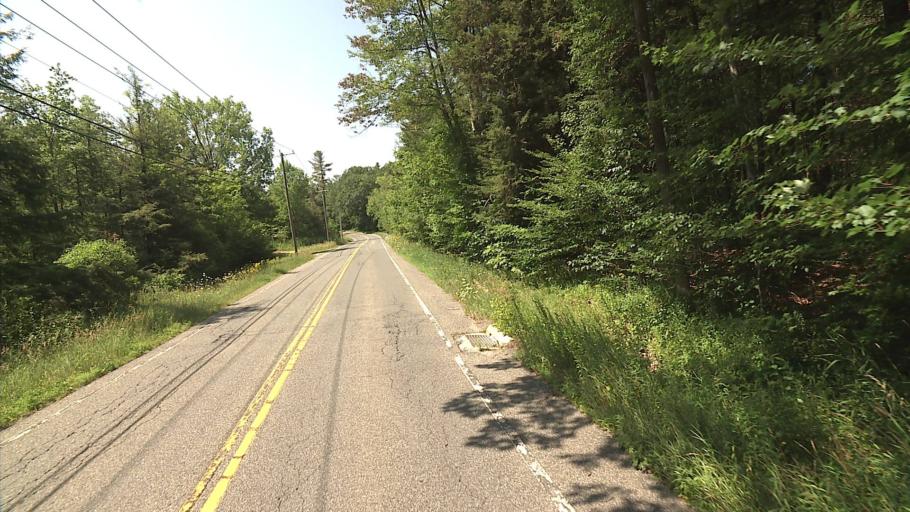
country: US
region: Connecticut
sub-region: Litchfield County
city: Winchester Center
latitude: 41.9506
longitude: -73.2073
